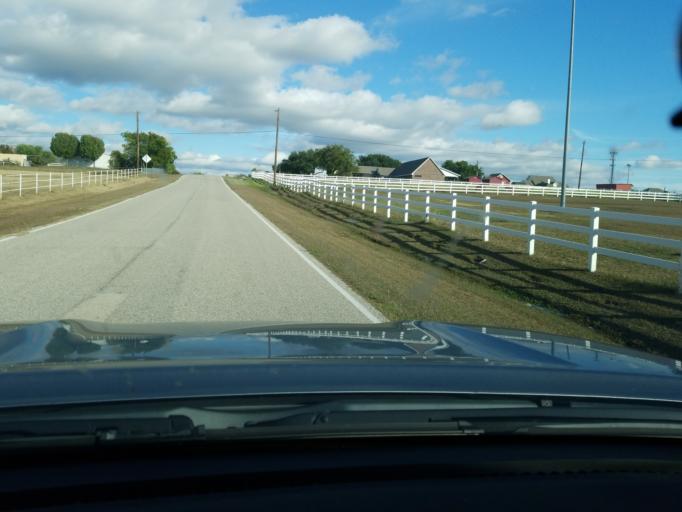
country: US
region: Texas
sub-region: Tarrant County
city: Pecan Acres
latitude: 32.9726
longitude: -97.4151
